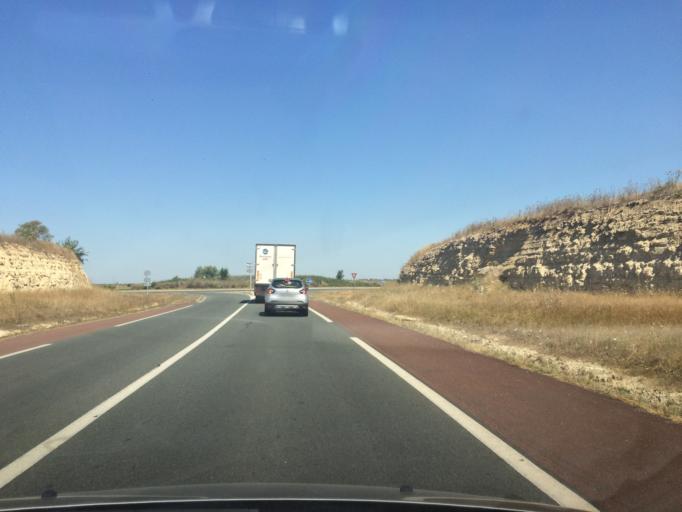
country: FR
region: Poitou-Charentes
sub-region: Departement de la Charente-Maritime
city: Esnandes
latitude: 46.2416
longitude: -1.0786
